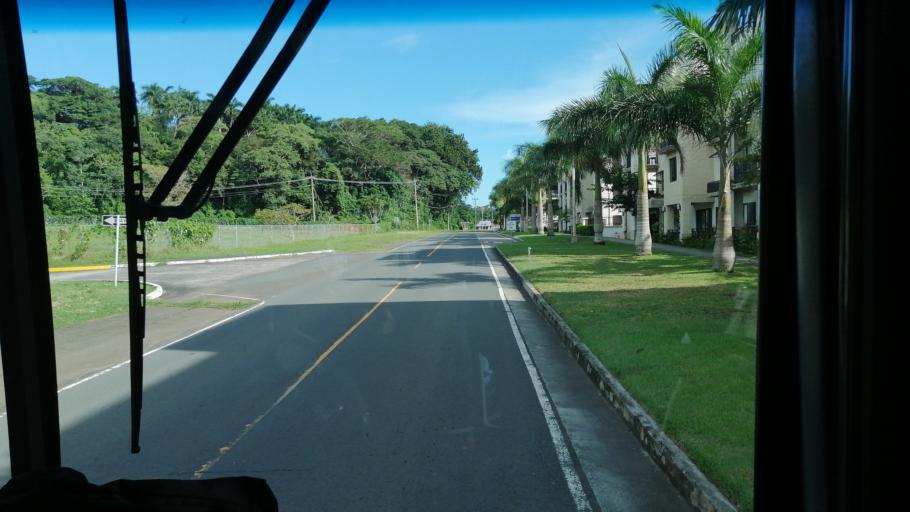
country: PA
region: Panama
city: Veracruz
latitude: 8.9055
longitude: -79.5897
